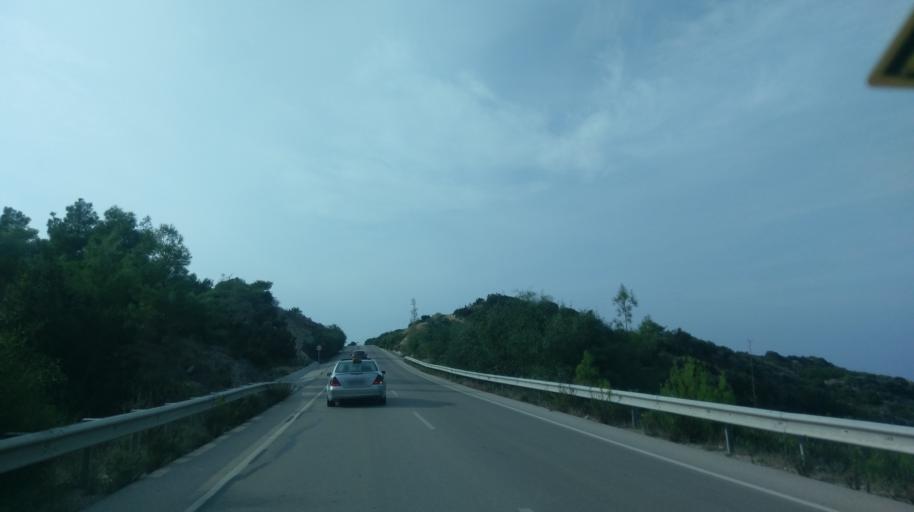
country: CY
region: Ammochostos
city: Trikomo
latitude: 35.4106
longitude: 33.8086
